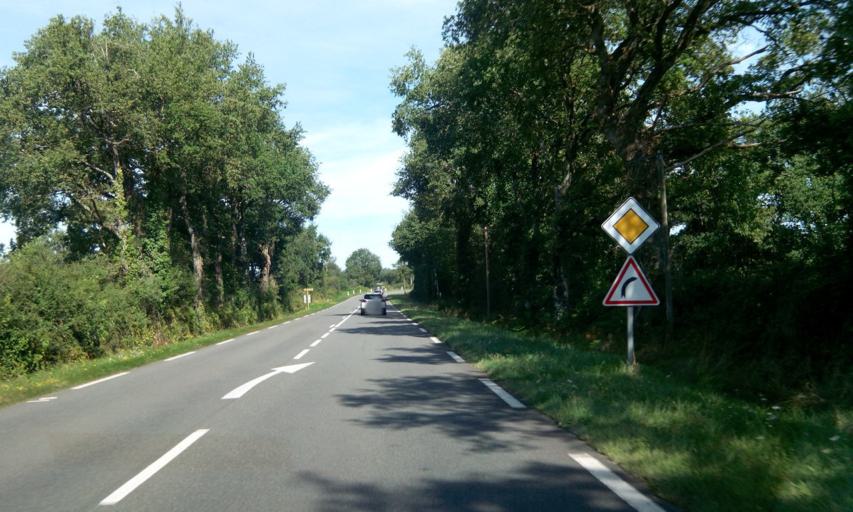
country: FR
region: Poitou-Charentes
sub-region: Departement de la Vienne
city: Availles-Limouzine
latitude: 46.0692
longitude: 0.5956
